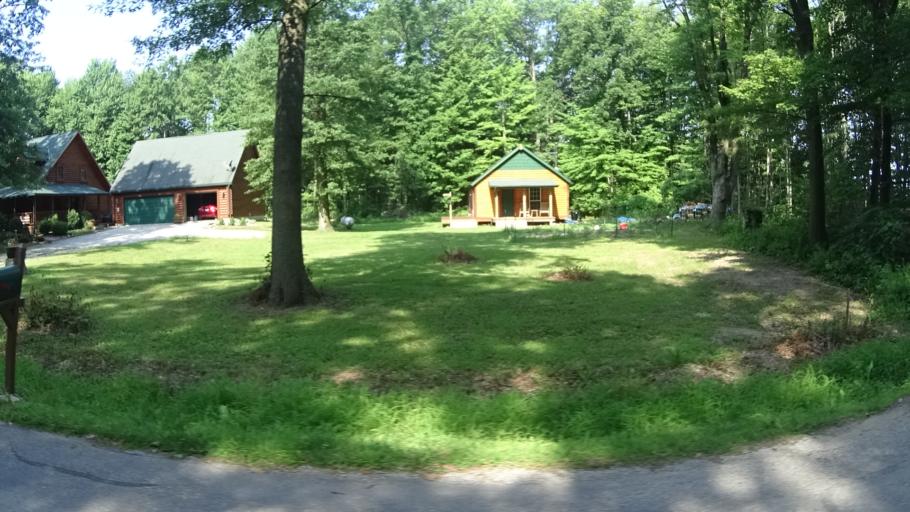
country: US
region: Ohio
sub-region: Lorain County
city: Vermilion
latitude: 41.3749
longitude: -82.4307
